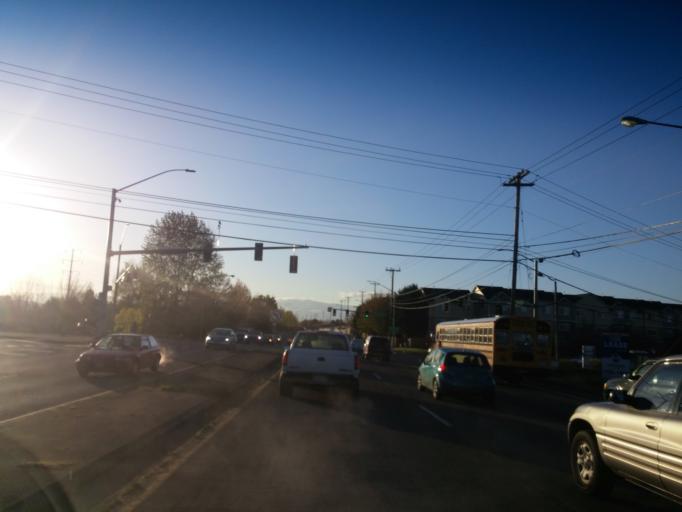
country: US
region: Oregon
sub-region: Washington County
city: Aloha
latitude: 45.5158
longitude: -122.8682
